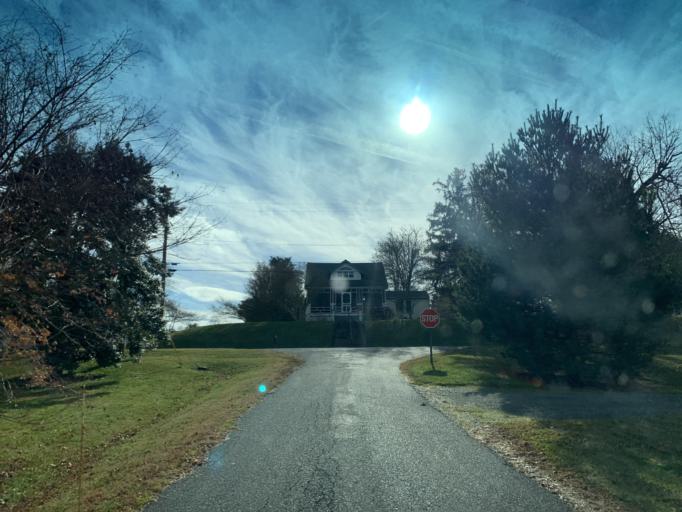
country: US
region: Maryland
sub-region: Harford County
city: Aberdeen Proving Ground
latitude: 39.3697
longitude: -76.0599
